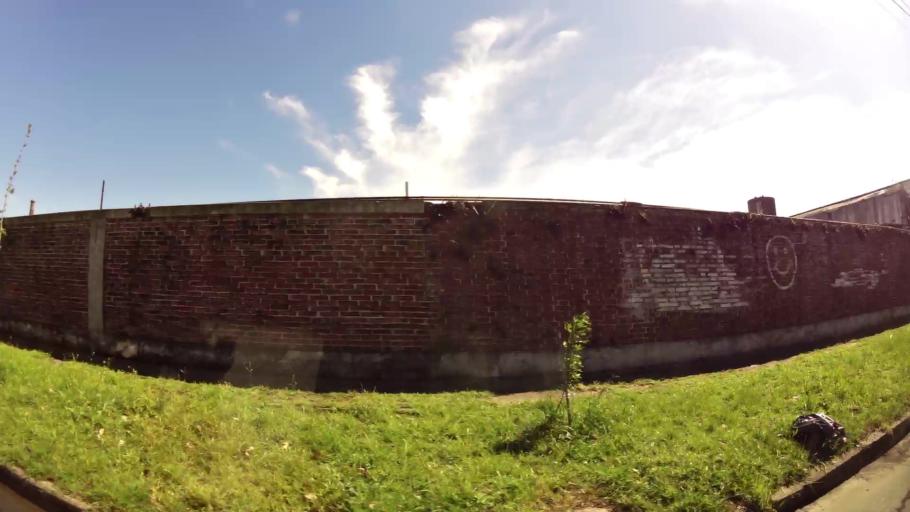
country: AR
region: Buenos Aires
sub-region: Partido de Quilmes
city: Quilmes
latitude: -34.7002
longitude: -58.2979
